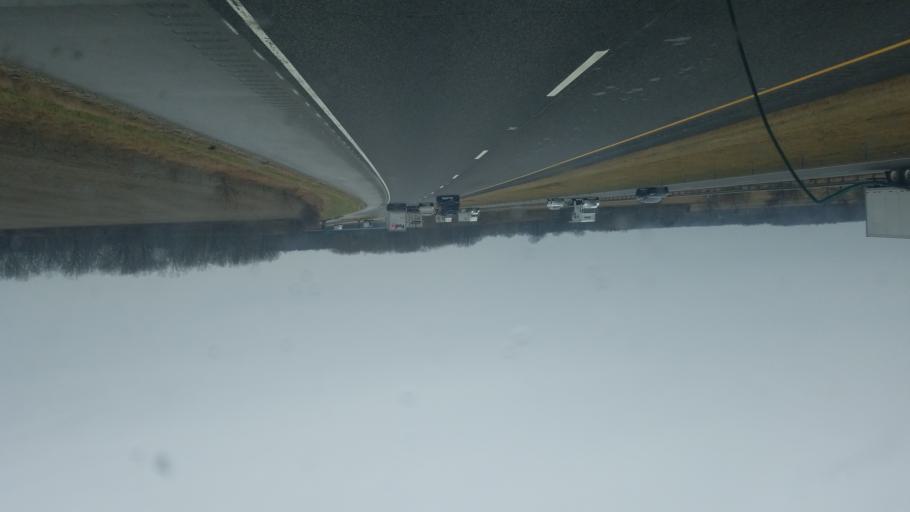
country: US
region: Indiana
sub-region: Wayne County
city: Centerville
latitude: 39.8538
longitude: -85.0659
